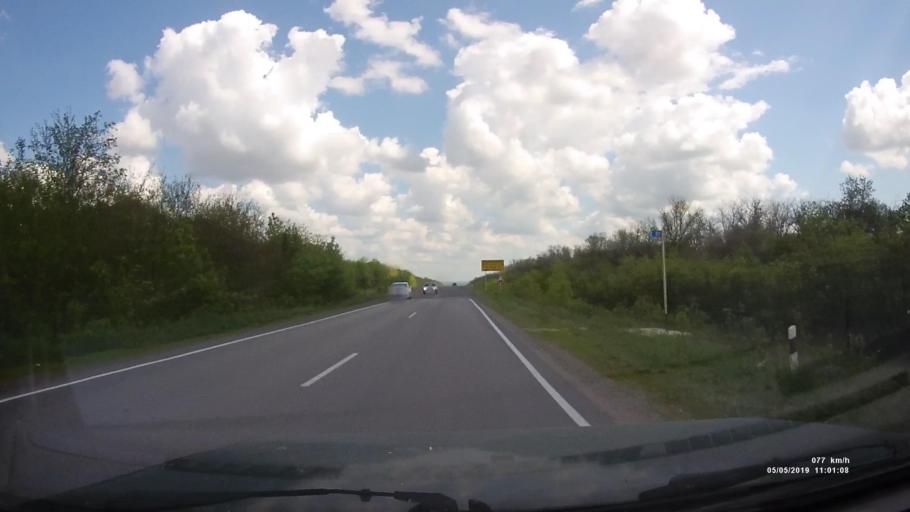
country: RU
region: Rostov
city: Ust'-Donetskiy
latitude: 47.6776
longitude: 40.8958
